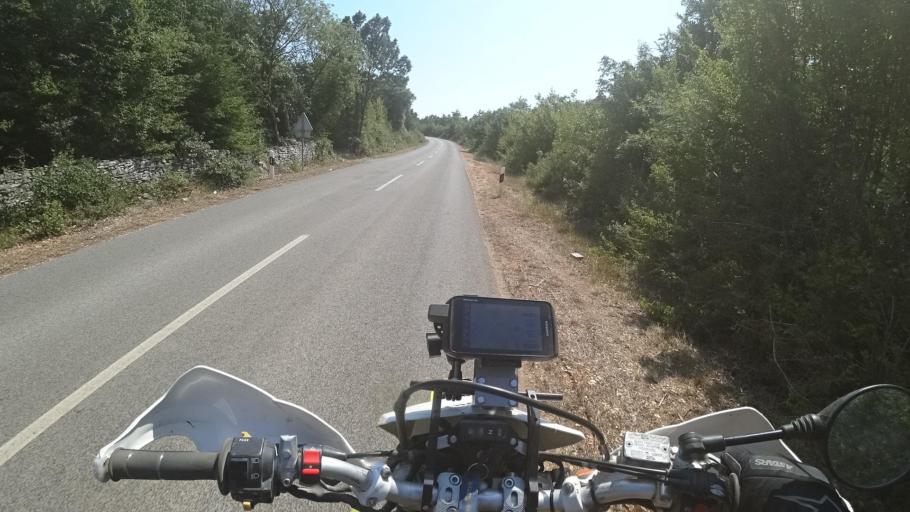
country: HR
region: Istarska
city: Fazana
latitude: 45.0053
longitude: 13.7793
